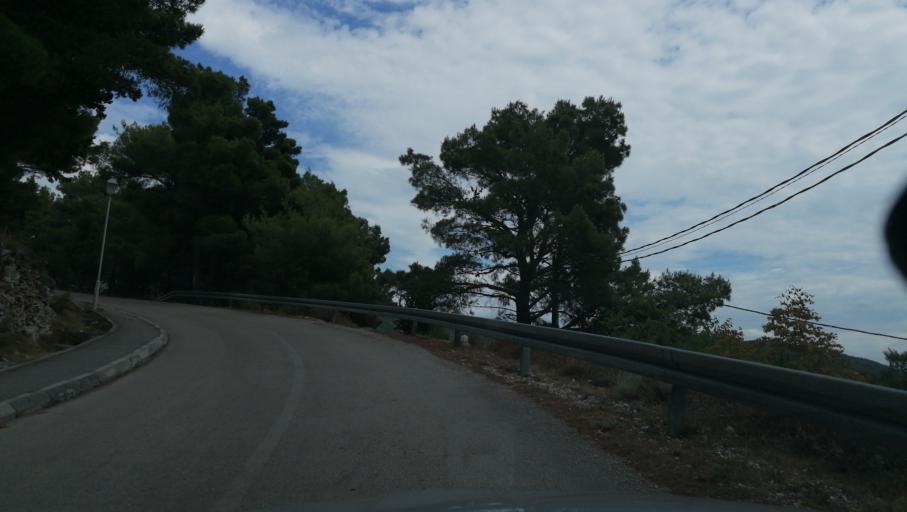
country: BA
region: Republika Srpska
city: Trebinje
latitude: 42.7083
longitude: 18.3623
